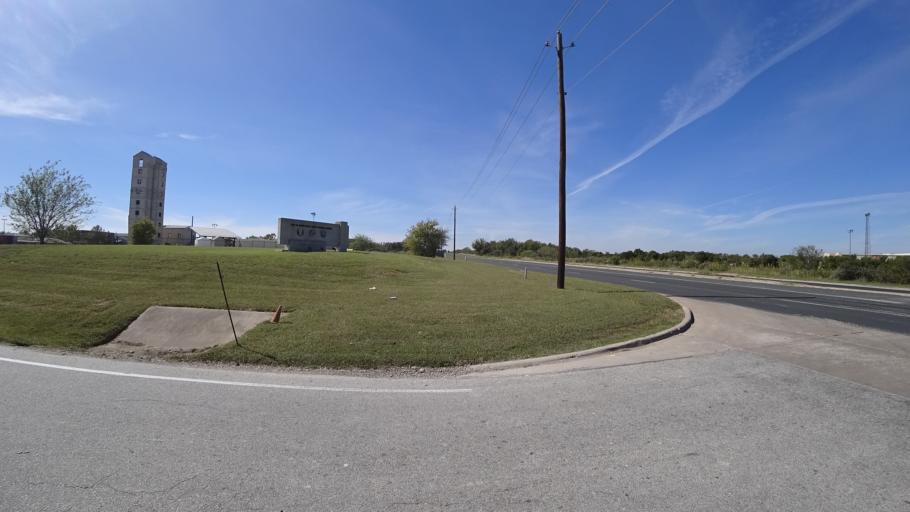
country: US
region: Texas
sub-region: Travis County
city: Austin
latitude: 30.1896
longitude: -97.7030
